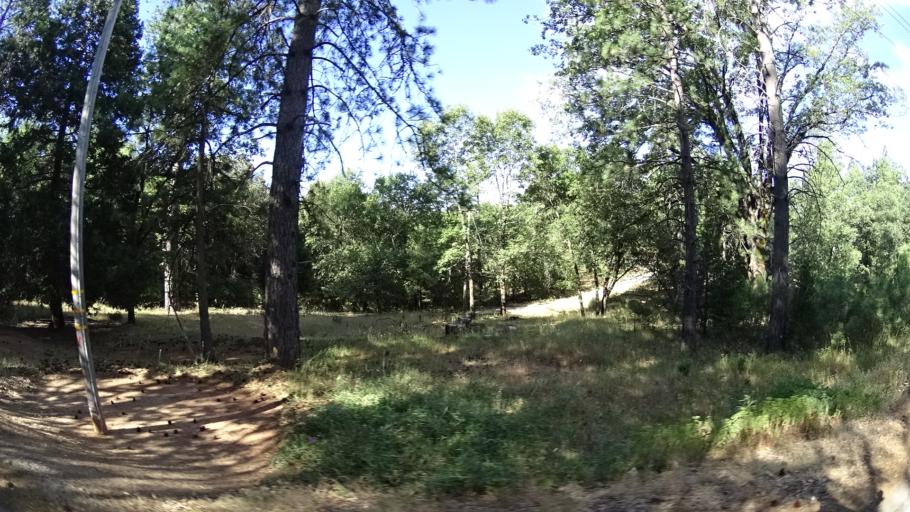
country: US
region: California
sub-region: Amador County
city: Pioneer
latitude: 38.3820
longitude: -120.5249
